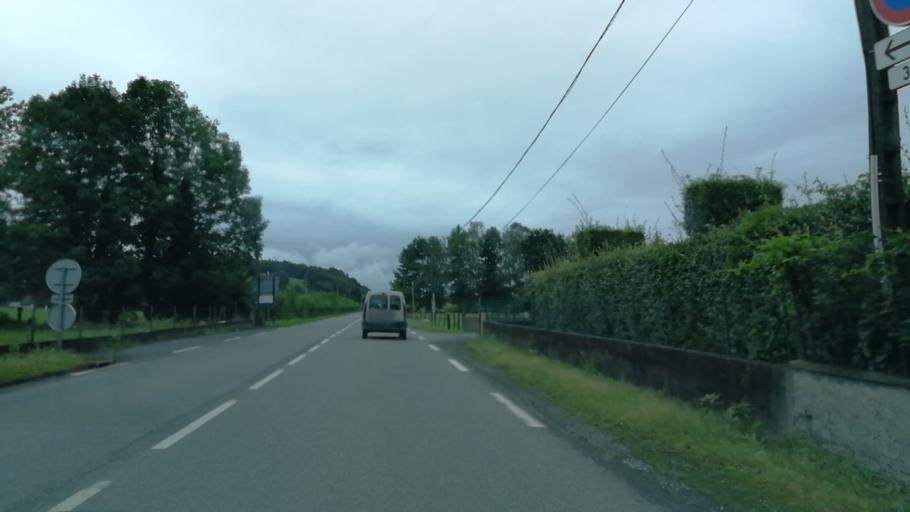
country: FR
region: Aquitaine
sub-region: Departement des Pyrenees-Atlantiques
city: Oloron-Sainte-Marie
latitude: 43.1251
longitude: -0.6121
